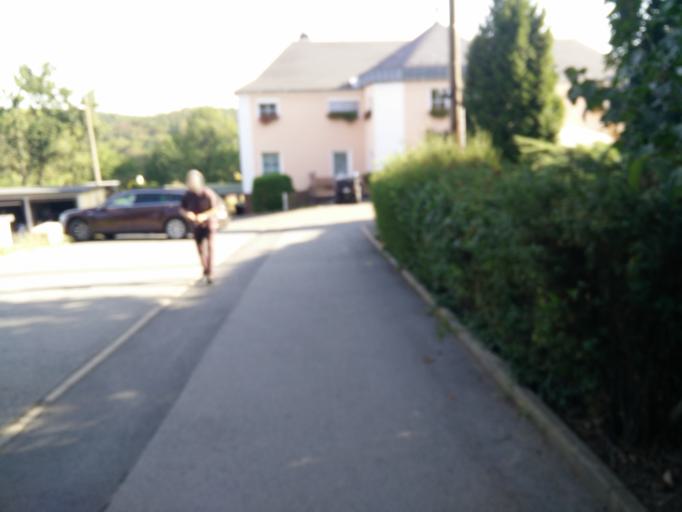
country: DE
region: Saxony
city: Rabenau
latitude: 50.9671
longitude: 13.6434
